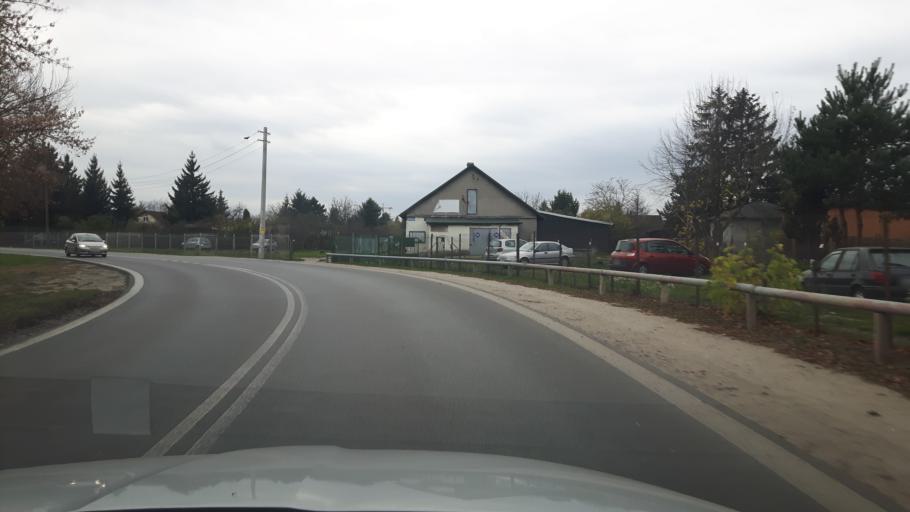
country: PL
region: Masovian Voivodeship
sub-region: Powiat wolominski
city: Zabki
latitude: 52.2838
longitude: 21.0970
